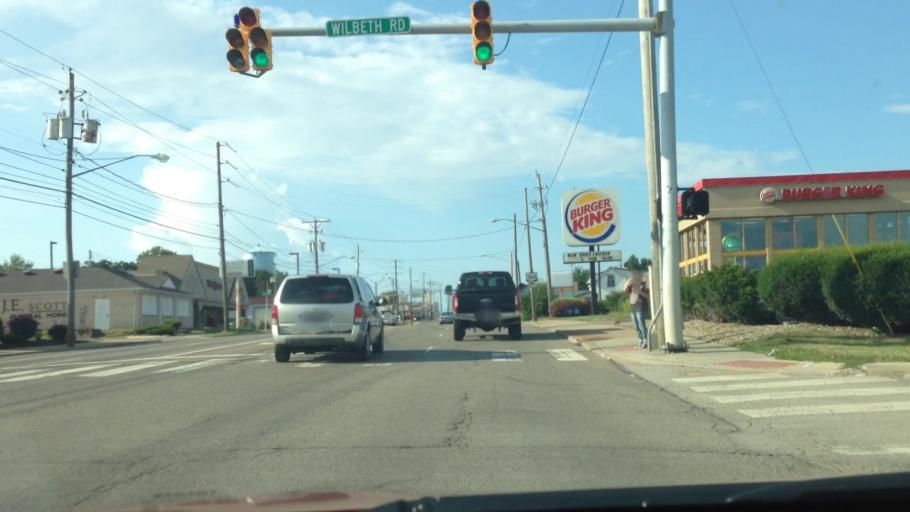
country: US
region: Ohio
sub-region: Summit County
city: Portage Lakes
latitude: 41.0398
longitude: -81.4912
